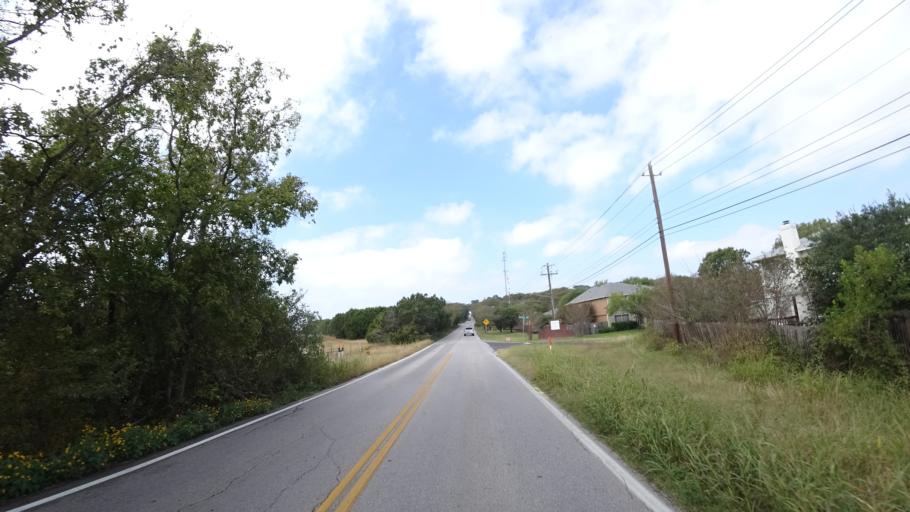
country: US
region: Texas
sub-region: Travis County
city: Shady Hollow
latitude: 30.1921
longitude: -97.8358
